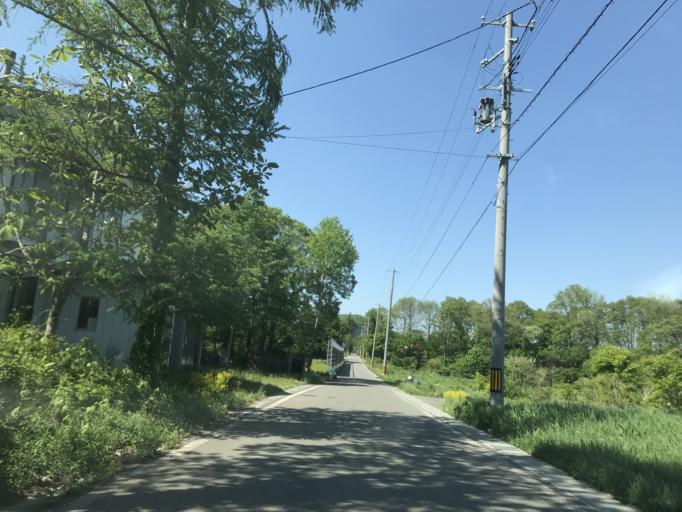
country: JP
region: Iwate
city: Shizukuishi
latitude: 39.5554
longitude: 140.8307
